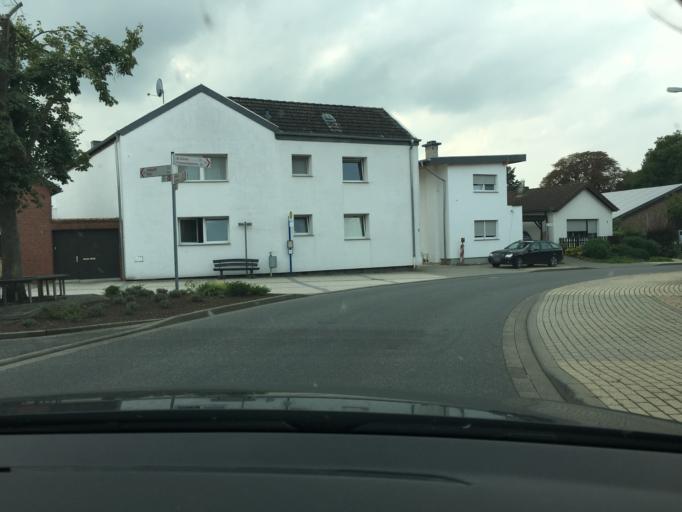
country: DE
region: North Rhine-Westphalia
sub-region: Regierungsbezirk Koln
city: Norvenich
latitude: 50.7905
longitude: 6.6213
